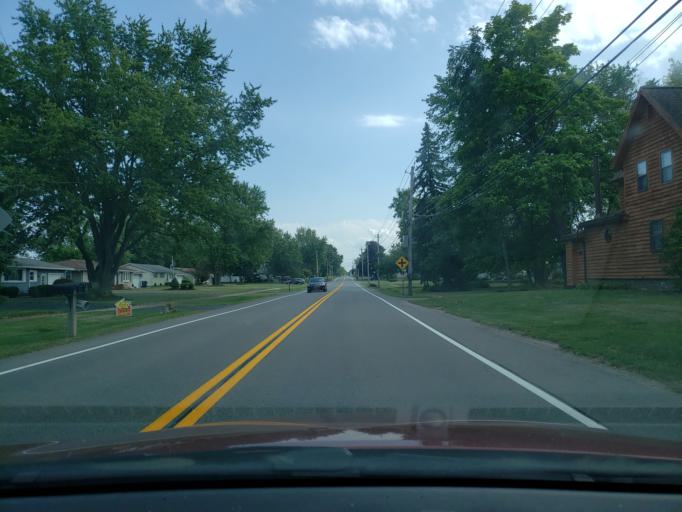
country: US
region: New York
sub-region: Monroe County
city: Greece
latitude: 43.2745
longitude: -77.7149
